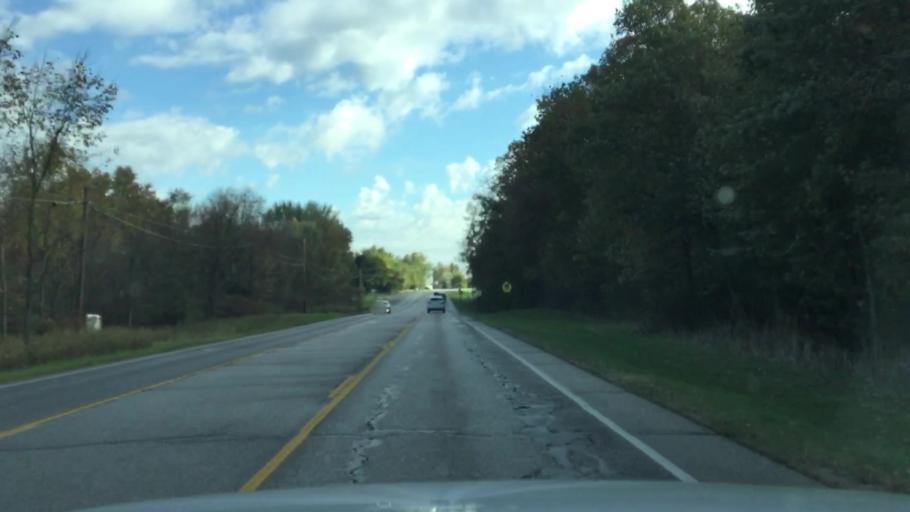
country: US
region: Michigan
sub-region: Lapeer County
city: Lapeer
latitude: 43.0478
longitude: -83.3512
